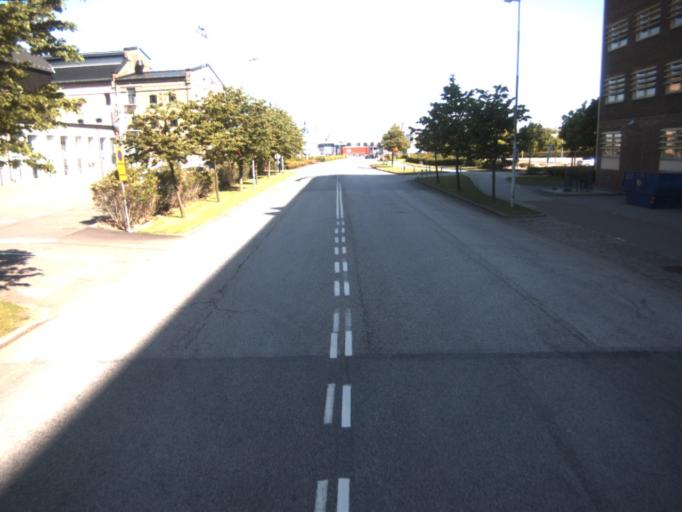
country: SE
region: Skane
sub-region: Helsingborg
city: Helsingborg
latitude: 56.0382
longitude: 12.6979
